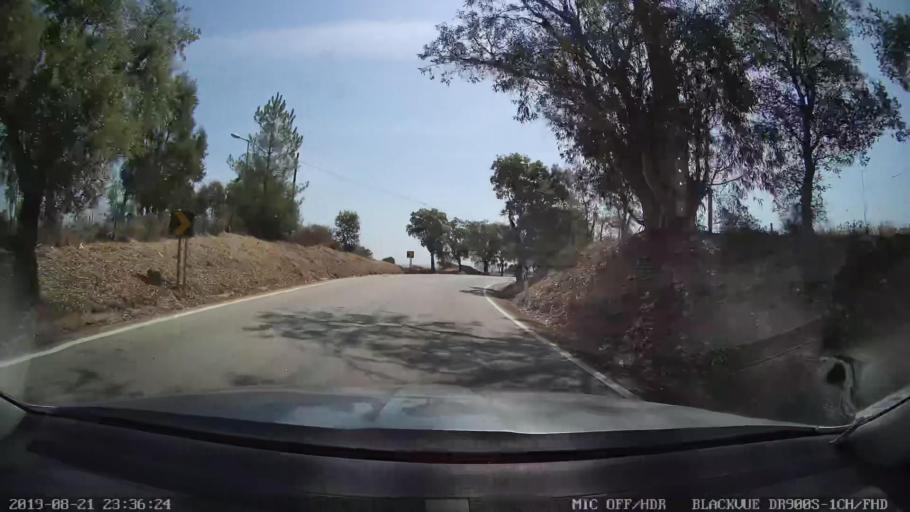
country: PT
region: Guarda
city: Alcains
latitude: 39.8760
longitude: -7.3751
